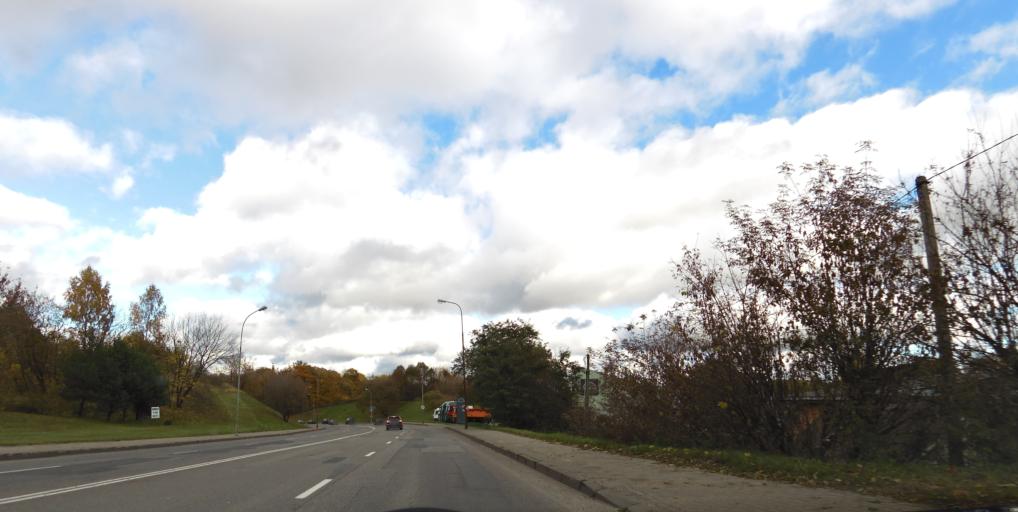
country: LT
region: Vilnius County
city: Rasos
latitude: 54.6644
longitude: 25.3043
